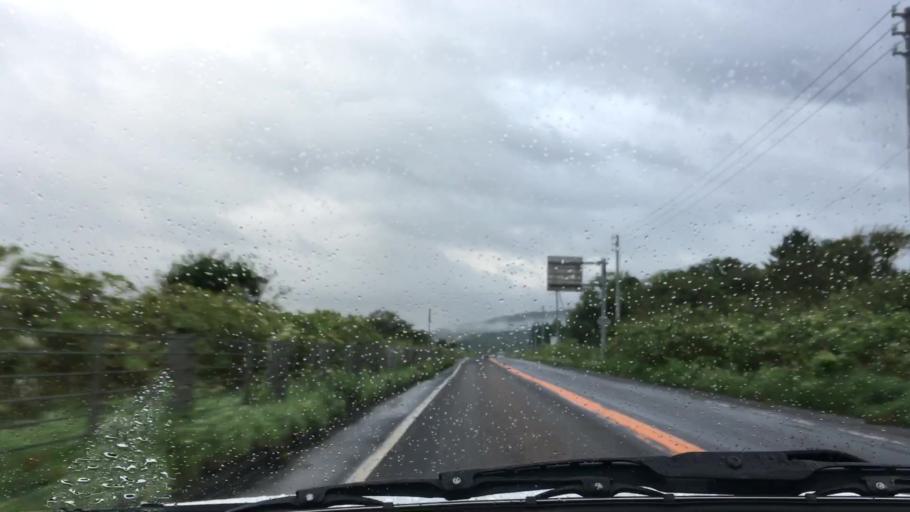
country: JP
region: Hokkaido
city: Nanae
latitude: 42.1857
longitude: 140.4367
